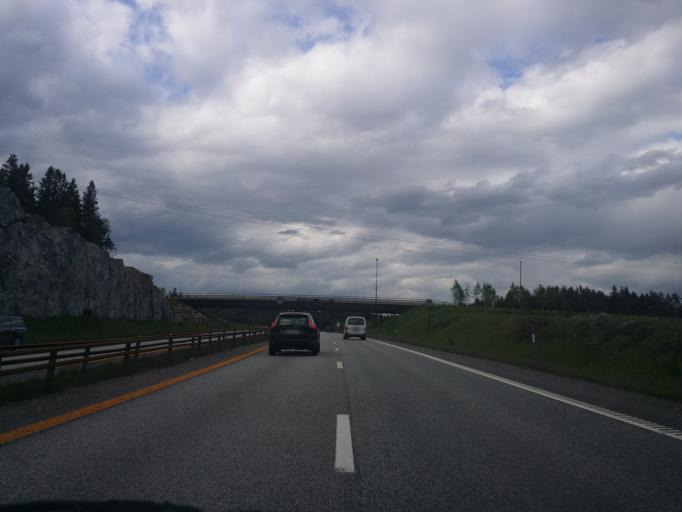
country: NO
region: Akershus
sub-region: Eidsvoll
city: Raholt
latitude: 60.3301
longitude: 11.1891
